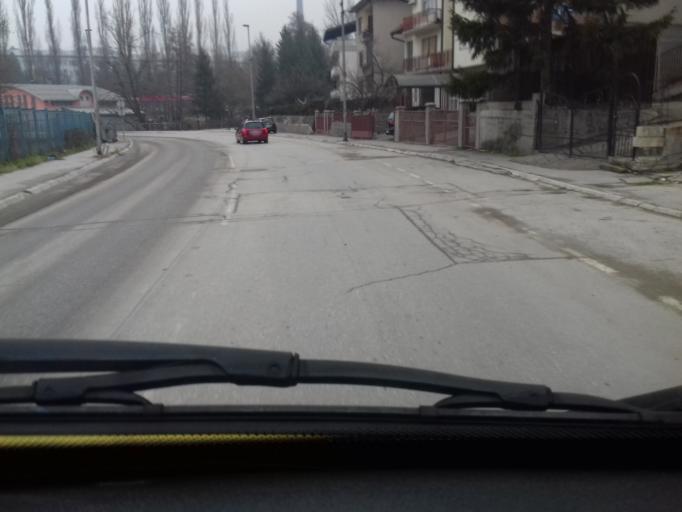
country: BA
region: Federation of Bosnia and Herzegovina
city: Zenica
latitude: 44.2070
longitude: 17.9278
